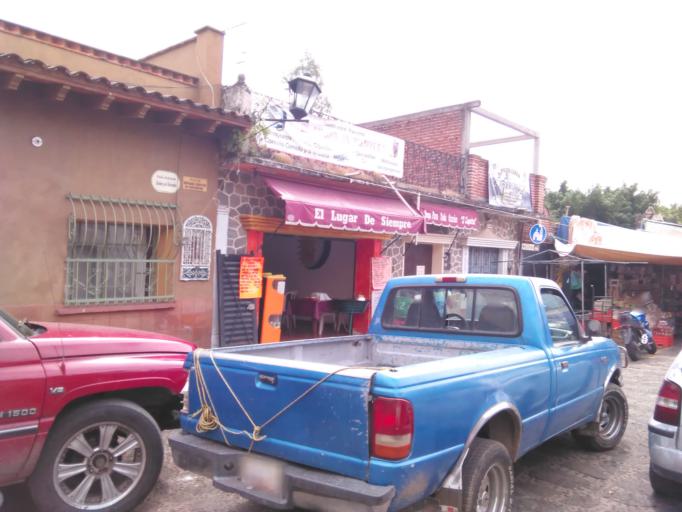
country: MX
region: Morelos
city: Tepoztlan
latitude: 18.9864
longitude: -99.1004
